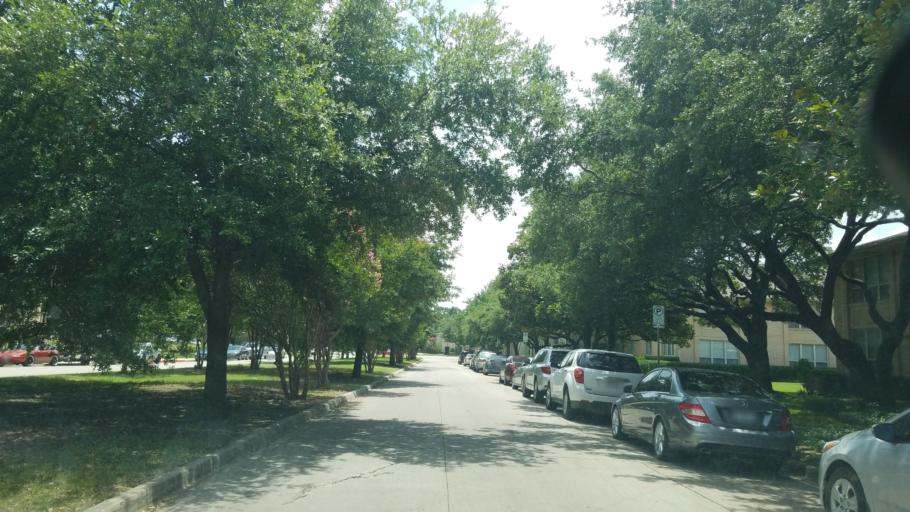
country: US
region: Texas
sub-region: Dallas County
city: University Park
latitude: 32.8672
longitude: -96.7955
